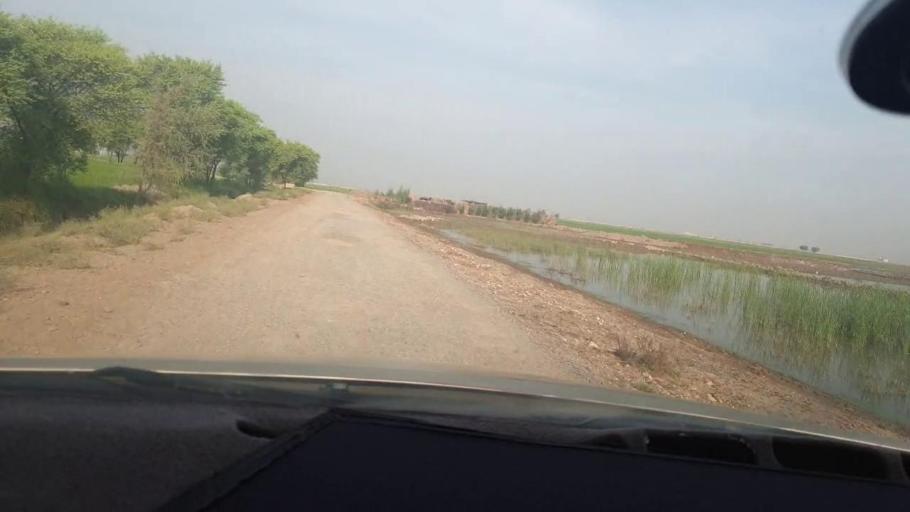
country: PK
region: Balochistan
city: Jhatpat
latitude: 28.3345
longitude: 68.3973
